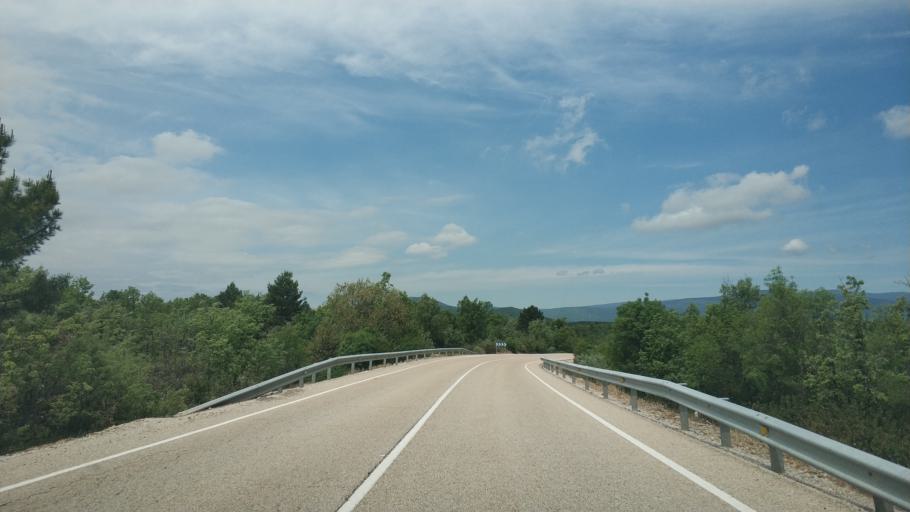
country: ES
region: Castille and Leon
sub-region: Provincia de Soria
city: Cidones
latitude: 41.8468
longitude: -2.5919
